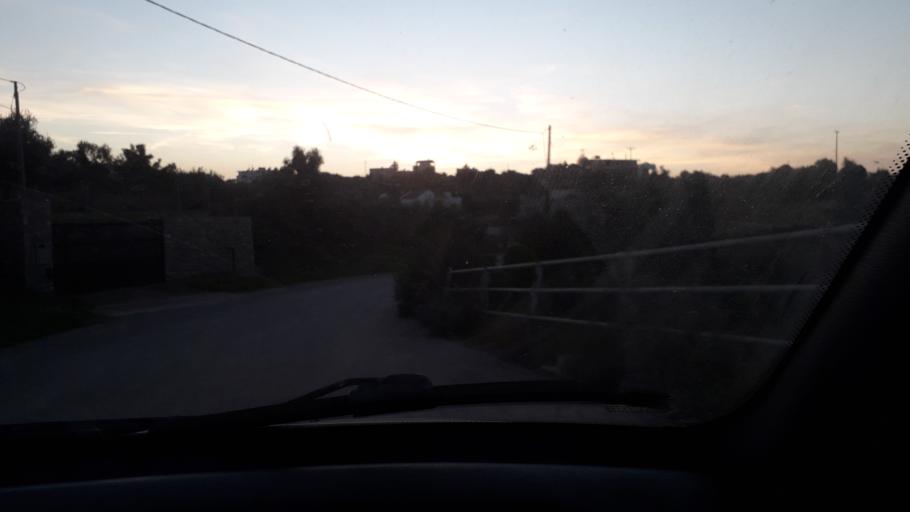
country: GR
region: Crete
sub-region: Nomos Rethymnis
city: Panormos
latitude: 35.3856
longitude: 24.6168
